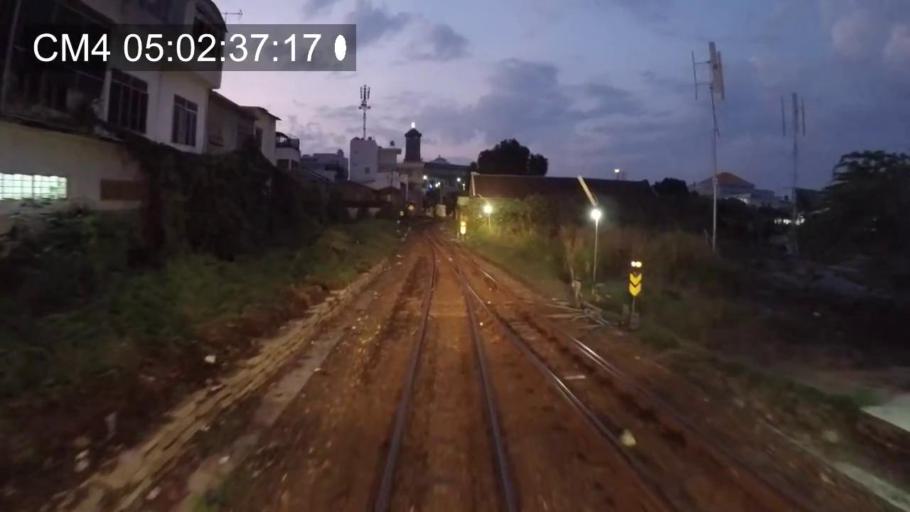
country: VN
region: Khanh Hoa
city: Nha Trang
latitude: 12.2513
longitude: 109.1746
